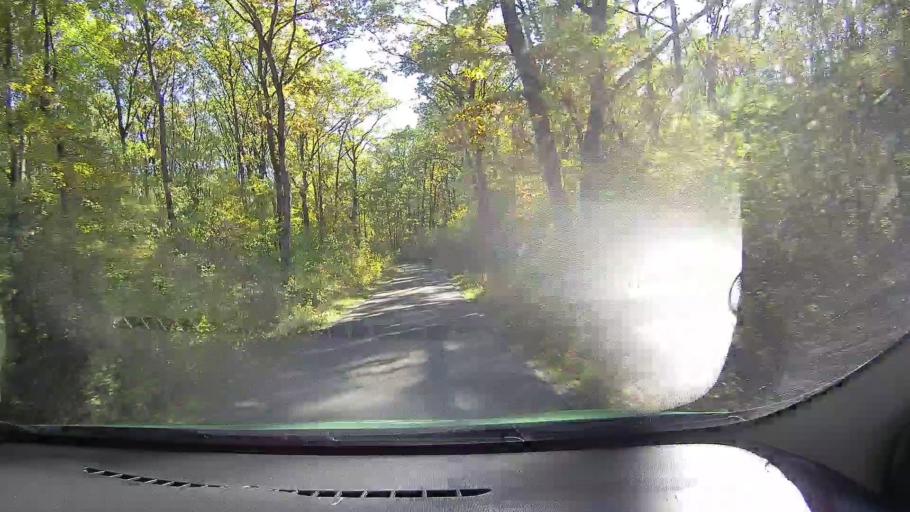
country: RO
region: Satu Mare
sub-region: Municipiul Satu Mare
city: Satmarel
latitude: 47.7061
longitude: 22.7616
